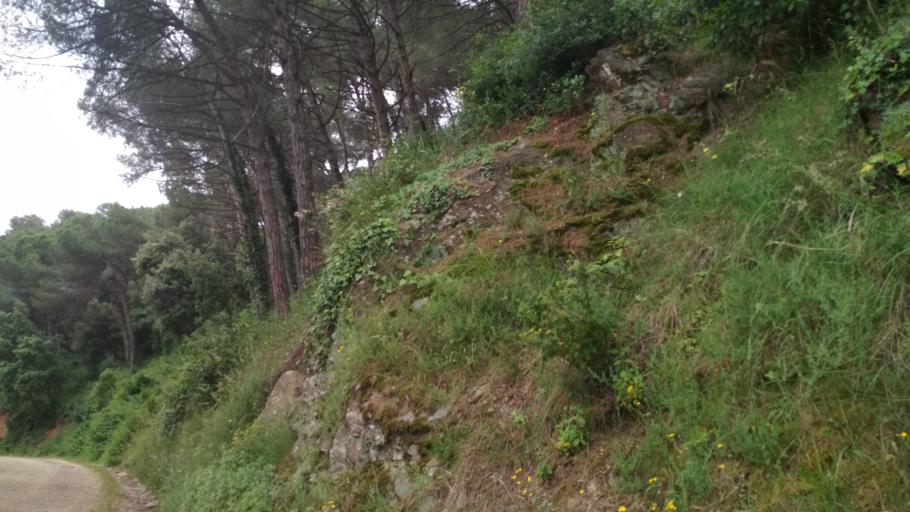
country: ES
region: Catalonia
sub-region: Provincia de Barcelona
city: Nou Barris
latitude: 41.4527
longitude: 2.1666
